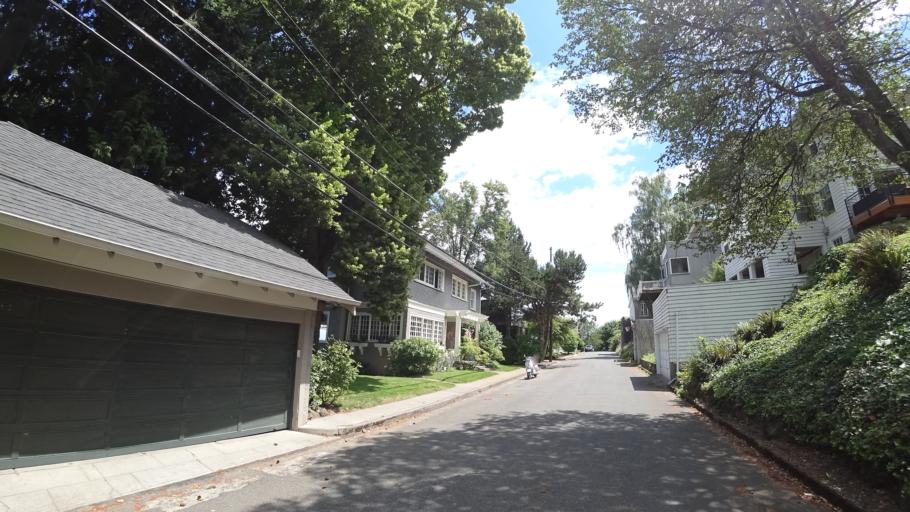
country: US
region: Oregon
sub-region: Multnomah County
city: Portland
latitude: 45.5325
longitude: -122.7094
